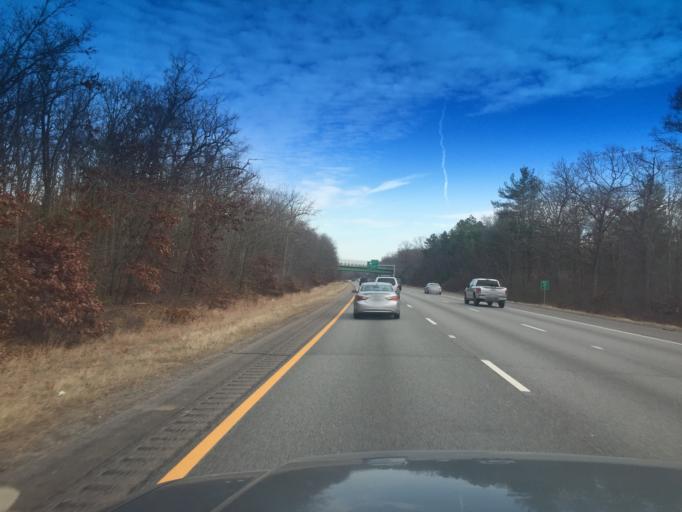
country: US
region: Massachusetts
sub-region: Norfolk County
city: Wrentham
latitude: 42.0372
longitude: -71.3237
